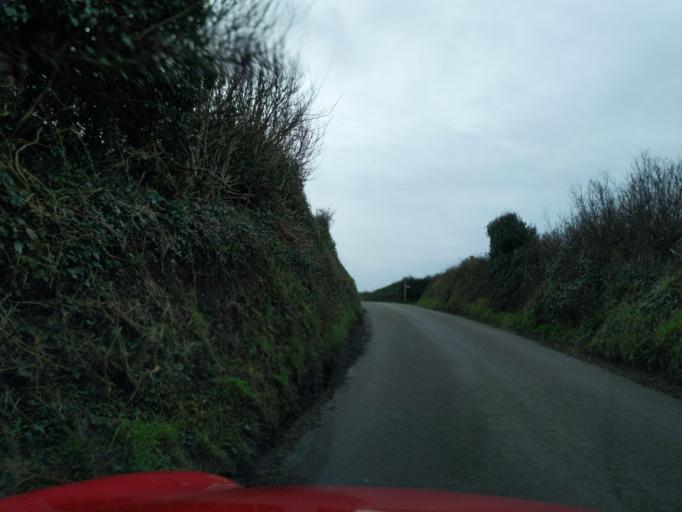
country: GB
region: England
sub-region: Cornwall
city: Fowey
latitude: 50.3288
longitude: -4.6231
